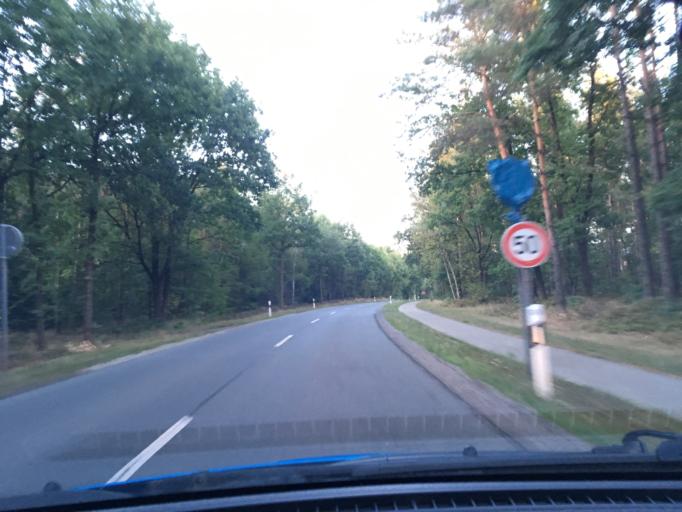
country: DE
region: Lower Saxony
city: Fassberg
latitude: 52.8872
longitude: 10.1442
